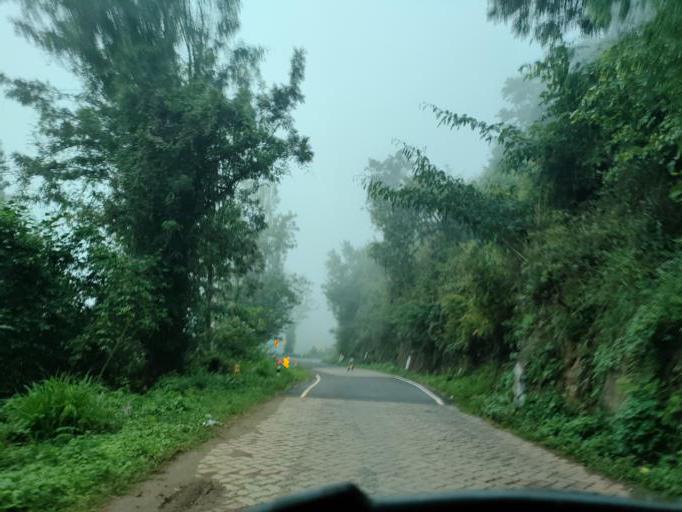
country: IN
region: Tamil Nadu
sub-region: Dindigul
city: Ayakudi
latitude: 10.3504
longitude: 77.5747
